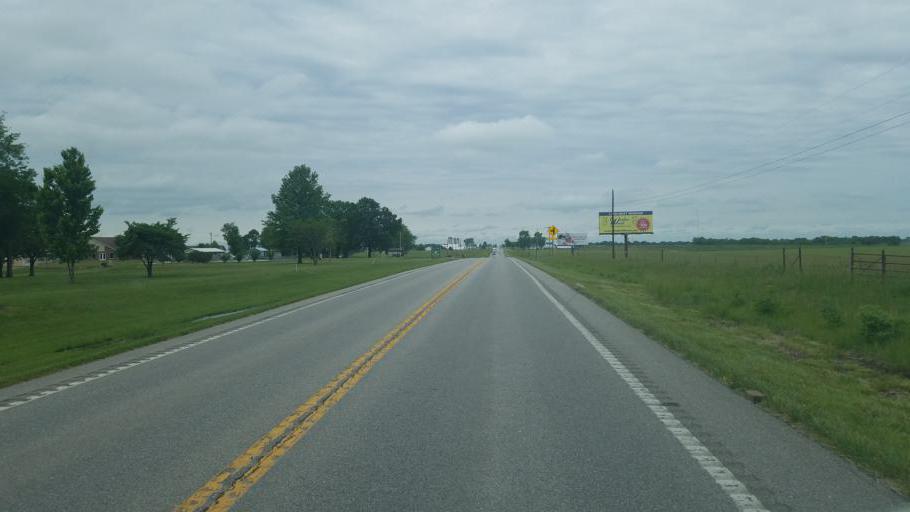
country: US
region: Missouri
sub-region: Morgan County
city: Versailles
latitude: 38.4689
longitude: -92.8088
